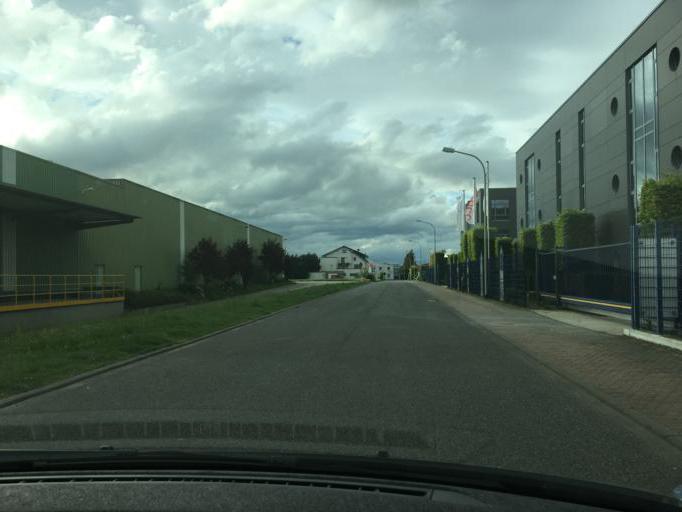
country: DE
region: North Rhine-Westphalia
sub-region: Regierungsbezirk Koln
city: Merzenich
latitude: 50.8143
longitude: 6.5459
